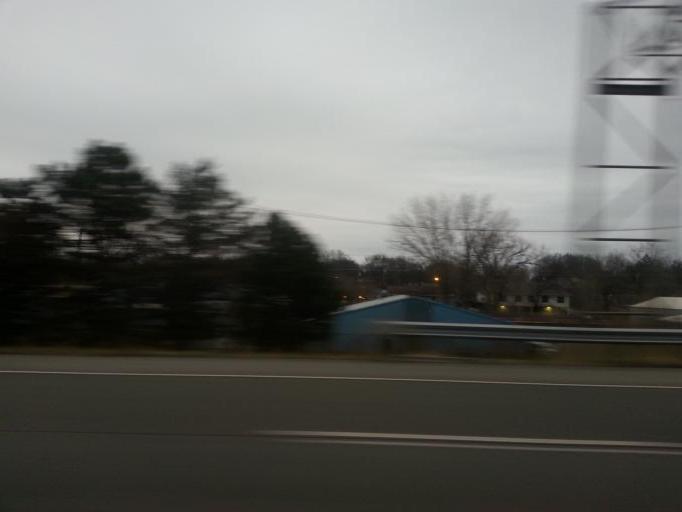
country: US
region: Iowa
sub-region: Linn County
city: Cedar Rapids
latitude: 42.0151
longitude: -91.6668
